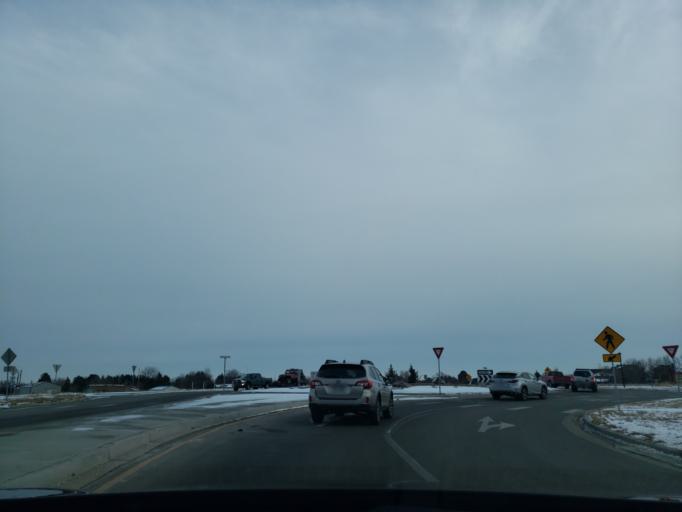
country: US
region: Colorado
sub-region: Larimer County
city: Campion
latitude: 40.3472
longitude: -105.0957
